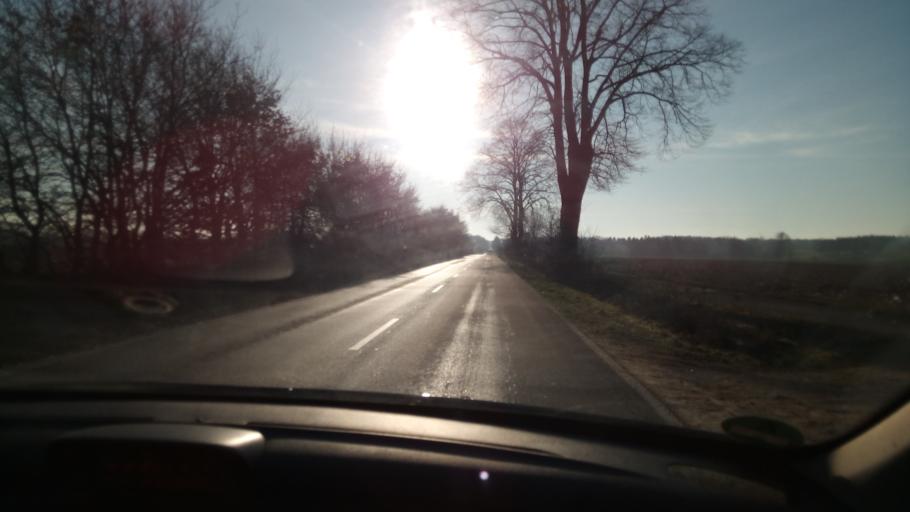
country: DE
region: Schleswig-Holstein
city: Witzeeze
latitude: 53.4456
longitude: 10.6096
